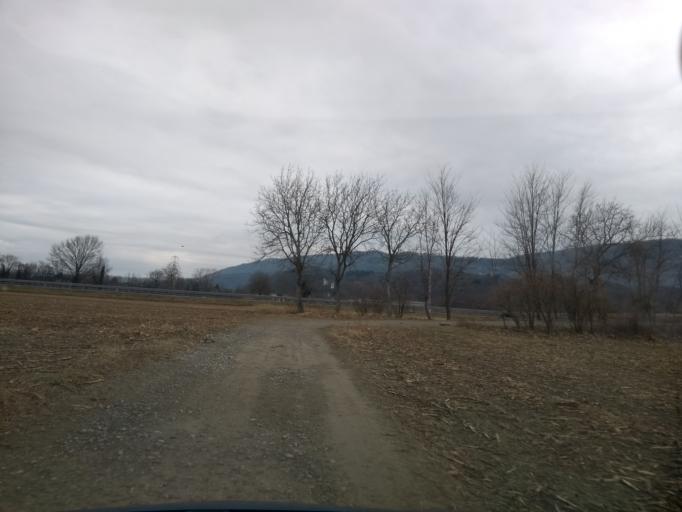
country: IT
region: Piedmont
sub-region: Provincia di Torino
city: Fiorano Canavese
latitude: 45.4753
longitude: 7.8420
